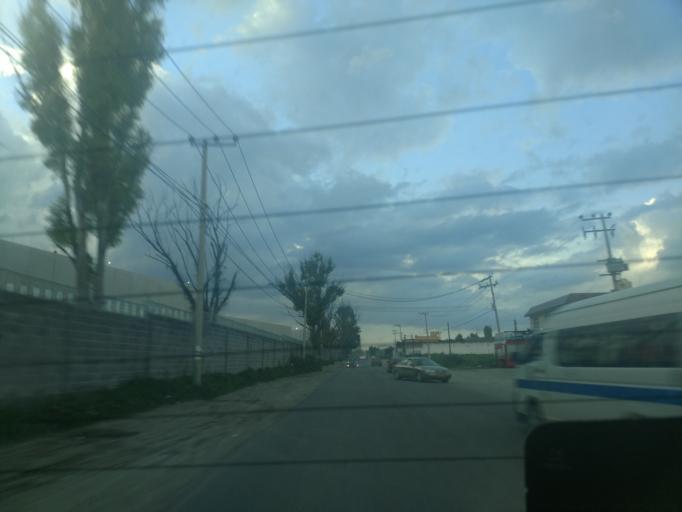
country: MX
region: Mexico
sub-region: Cuautitlan
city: Barrio Tlatenco
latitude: 19.7430
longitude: -99.1996
